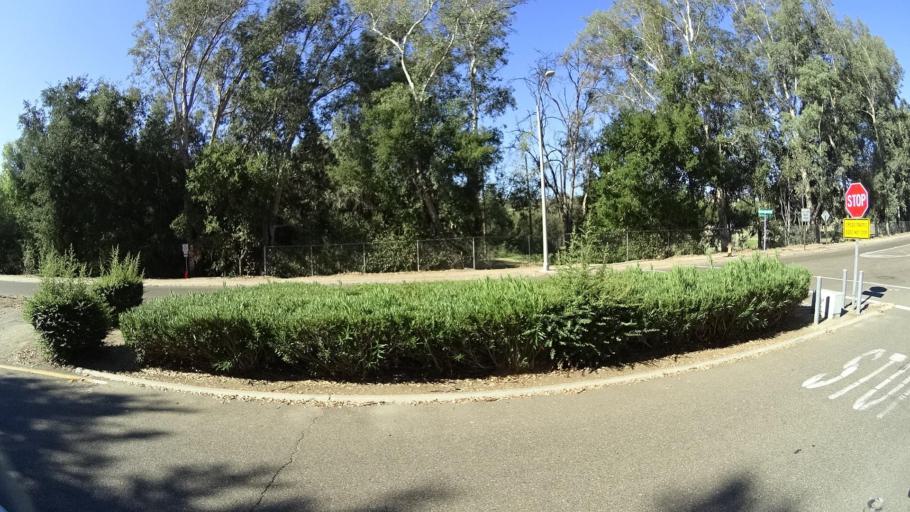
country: US
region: California
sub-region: San Diego County
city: San Diego Country Estates
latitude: 33.0016
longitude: -116.8023
